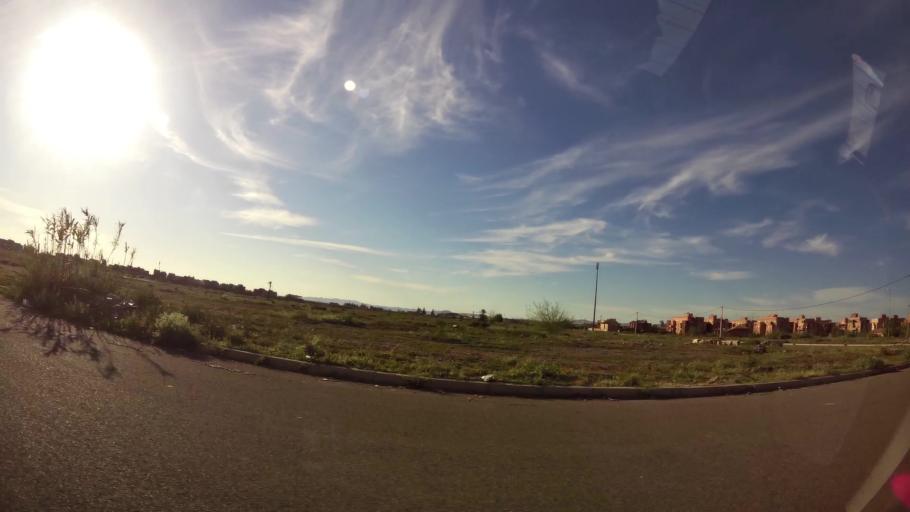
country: MA
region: Marrakech-Tensift-Al Haouz
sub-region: Marrakech
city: Marrakesh
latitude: 31.6739
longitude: -8.0661
